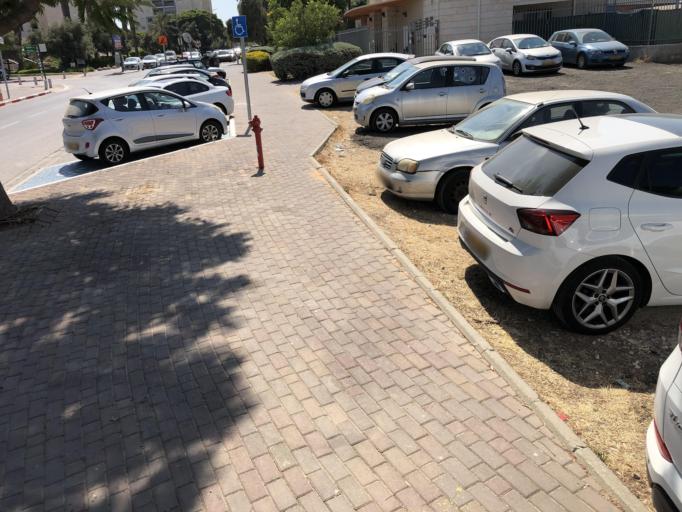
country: IL
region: Central District
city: Yehud
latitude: 32.0325
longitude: 34.8777
